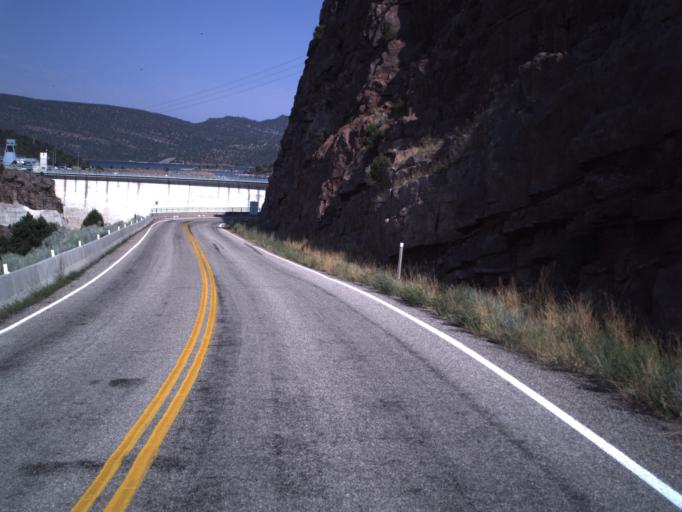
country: US
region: Utah
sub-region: Daggett County
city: Manila
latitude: 40.9126
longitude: -109.4182
